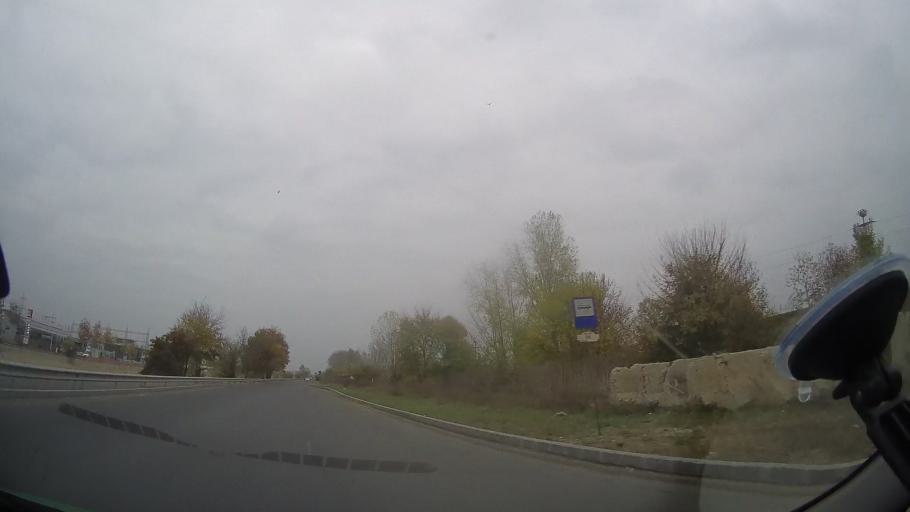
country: RO
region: Ilfov
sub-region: Comuna Popesti-Leordeni
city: Popesti-Leordeni
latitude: 44.3987
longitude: 26.1605
